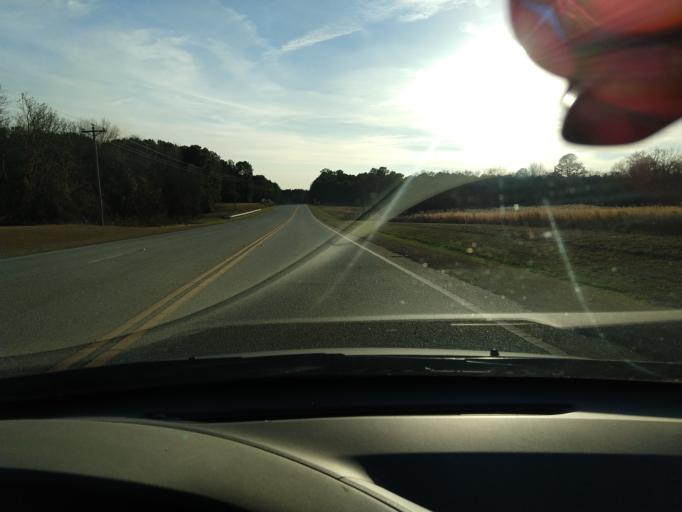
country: US
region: Georgia
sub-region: Sumter County
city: Americus
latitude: 32.1078
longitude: -84.1761
